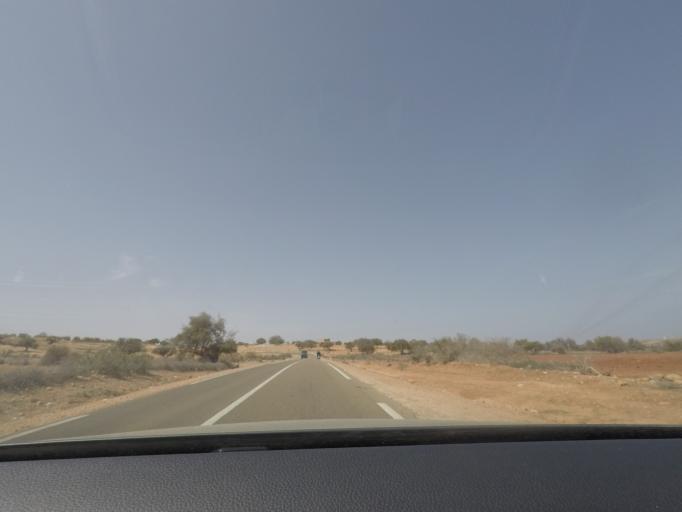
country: MA
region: Marrakech-Tensift-Al Haouz
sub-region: Essaouira
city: Tamanar
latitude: 31.0358
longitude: -9.6717
